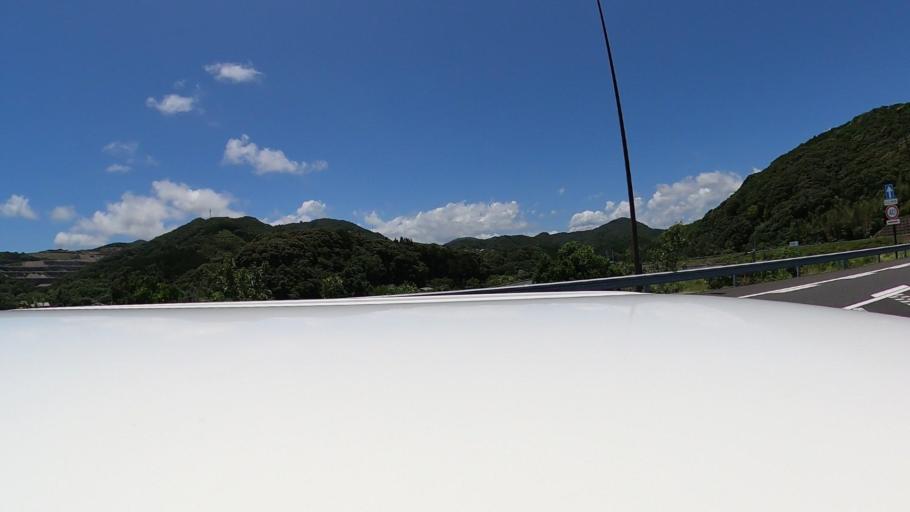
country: JP
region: Miyazaki
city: Nobeoka
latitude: 32.4002
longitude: 131.6169
